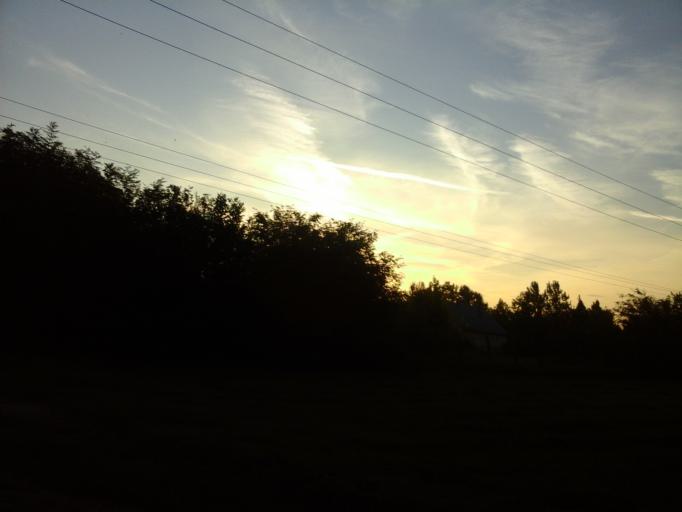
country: HU
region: Hajdu-Bihar
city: Hajduszoboszlo
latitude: 47.4620
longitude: 21.4162
